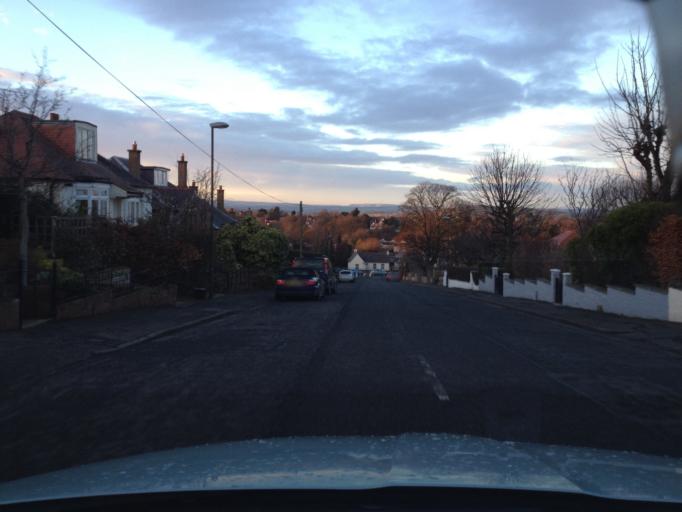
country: GB
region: Scotland
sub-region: Edinburgh
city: Colinton
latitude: 55.9015
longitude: -3.2684
